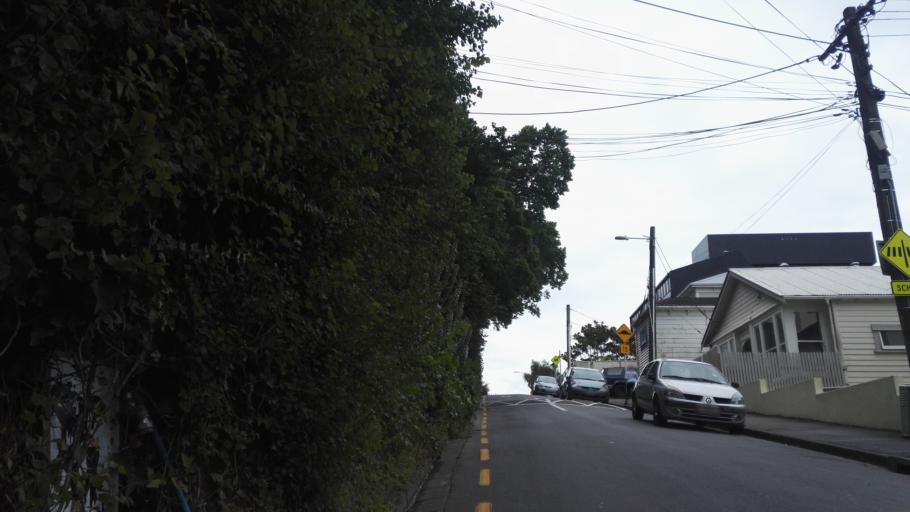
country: NZ
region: Wellington
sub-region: Wellington City
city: Wellington
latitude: -41.2944
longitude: 174.7689
